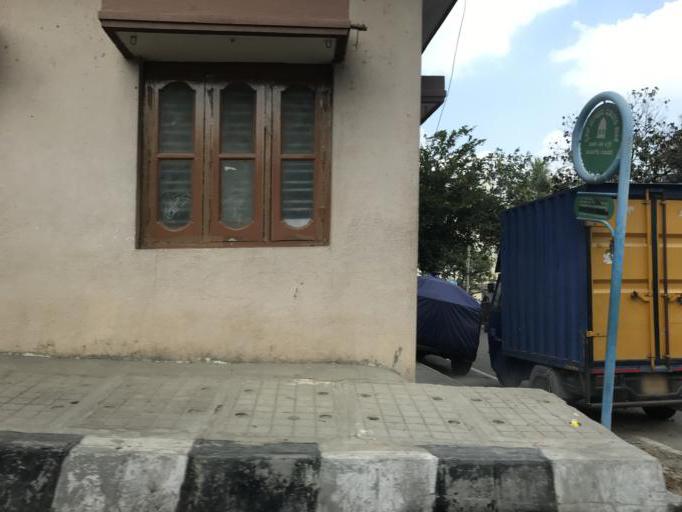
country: IN
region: Karnataka
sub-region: Bangalore Urban
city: Bangalore
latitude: 13.0004
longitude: 77.5262
